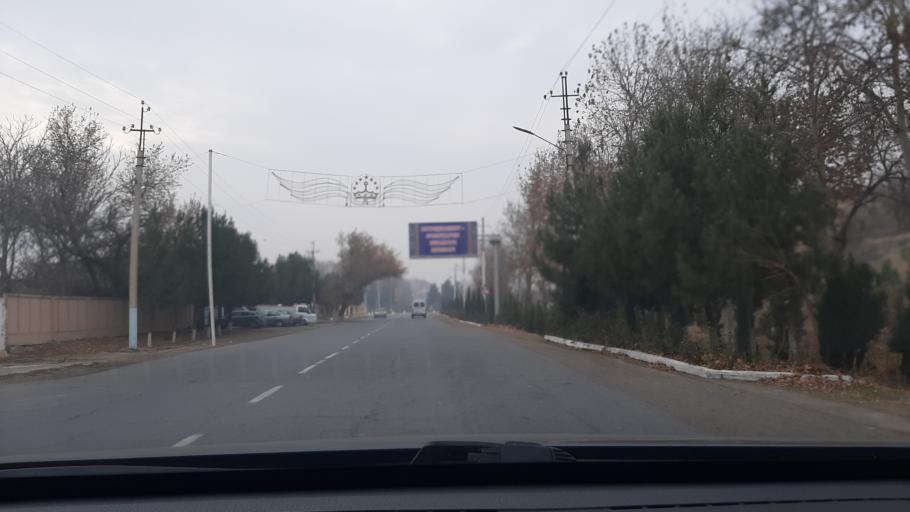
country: TJ
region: Viloyati Sughd
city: Palos
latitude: 40.2727
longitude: 69.8132
